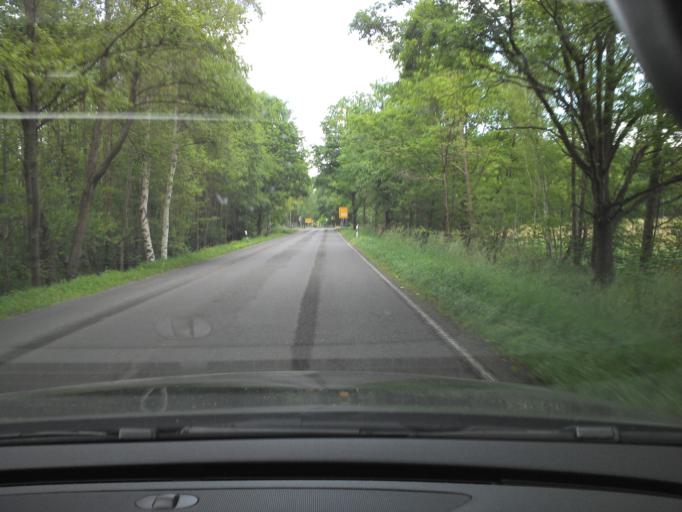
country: DE
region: Brandenburg
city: Burg
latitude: 51.8435
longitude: 14.1530
